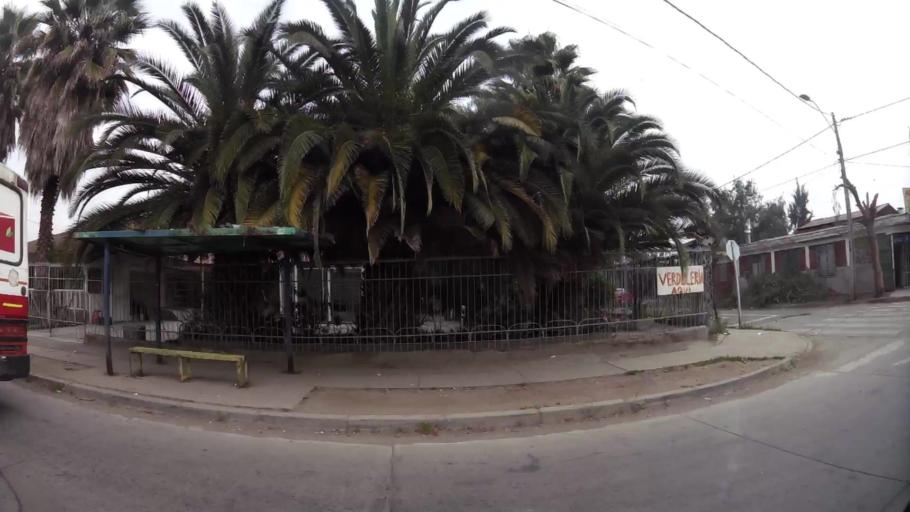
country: CL
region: Santiago Metropolitan
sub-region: Provincia de Chacabuco
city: Lampa
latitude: -33.2273
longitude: -70.8134
